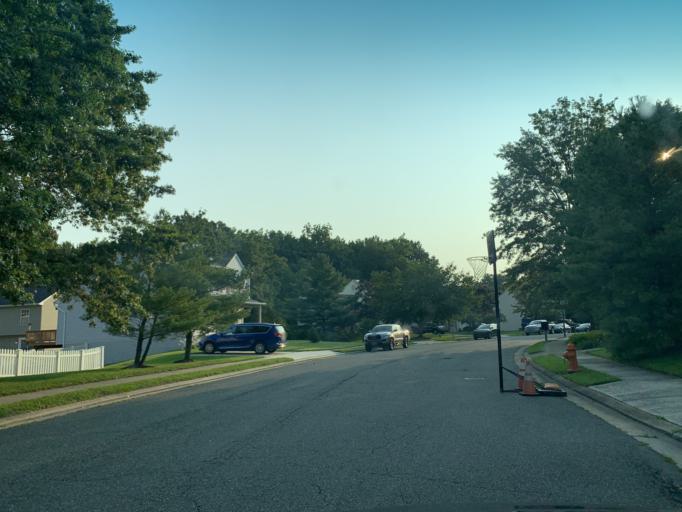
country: US
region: Maryland
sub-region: Baltimore County
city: Bowleys Quarters
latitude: 39.3680
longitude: -76.3656
